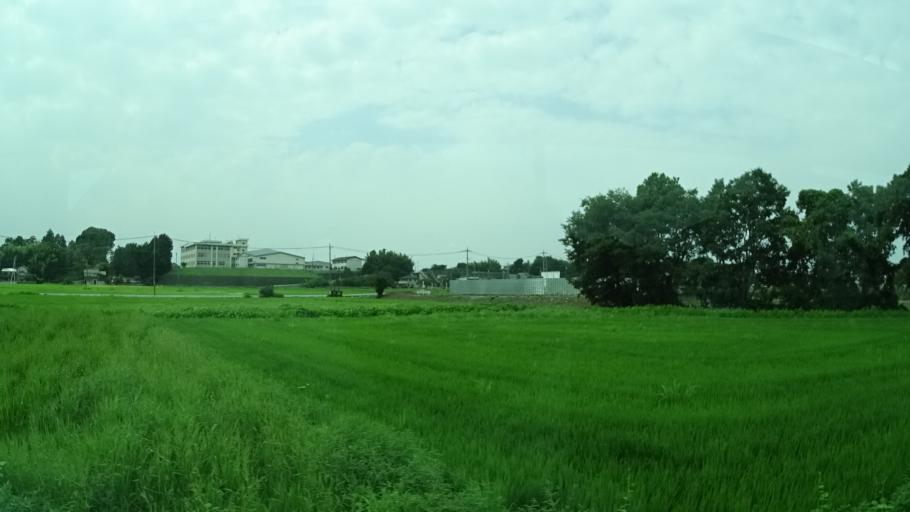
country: JP
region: Tochigi
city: Mooka
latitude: 36.4468
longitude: 140.0068
